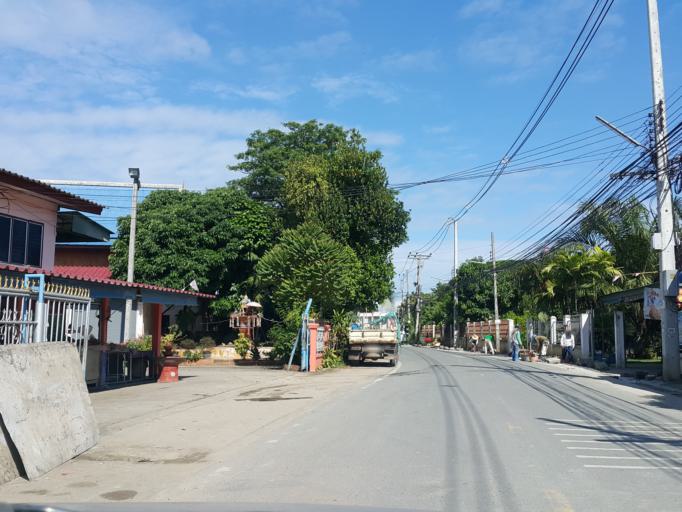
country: TH
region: Chiang Mai
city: San Sai
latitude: 18.7855
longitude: 99.0498
